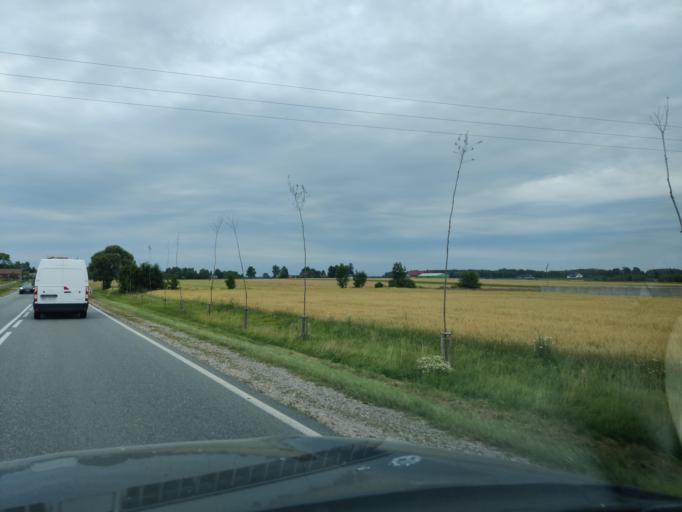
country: PL
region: Masovian Voivodeship
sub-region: Powiat minski
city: Stanislawow
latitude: 52.2371
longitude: 21.5418
